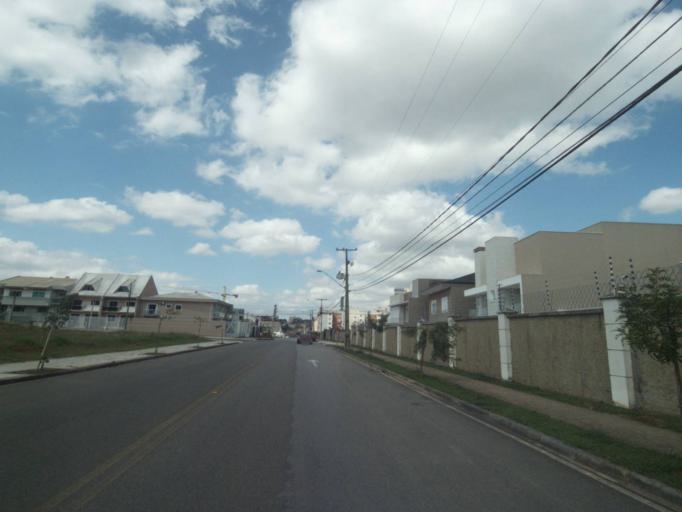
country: BR
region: Parana
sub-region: Curitiba
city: Curitiba
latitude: -25.5036
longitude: -49.3118
